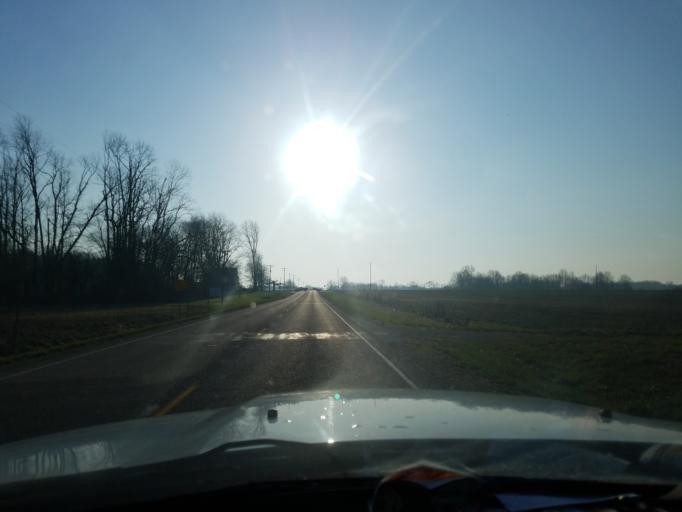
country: US
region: Indiana
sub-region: Vigo County
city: Seelyville
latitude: 39.3902
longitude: -87.2423
